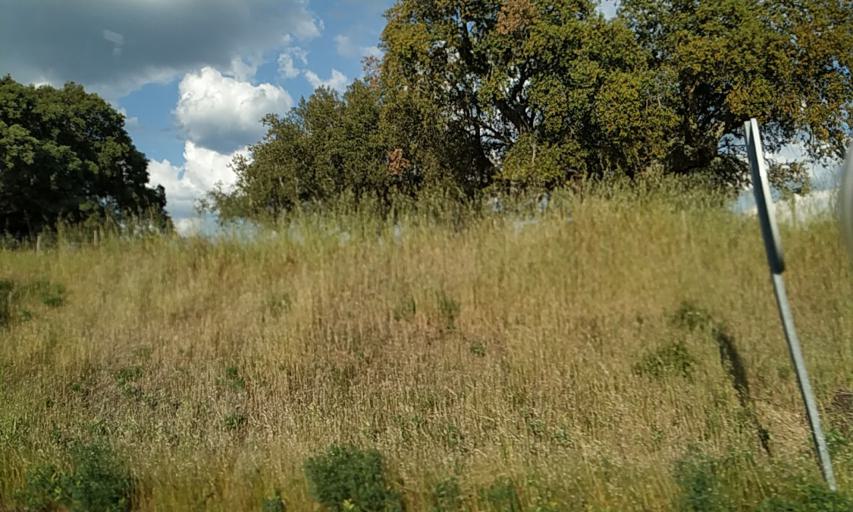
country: PT
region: Portalegre
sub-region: Portalegre
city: Urra
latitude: 39.2120
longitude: -7.4585
